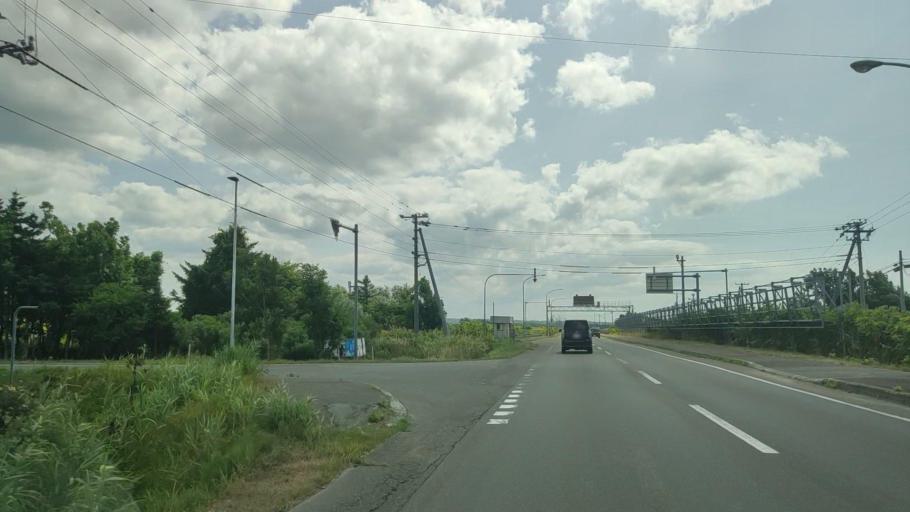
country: JP
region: Hokkaido
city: Makubetsu
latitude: 44.7556
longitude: 141.7947
